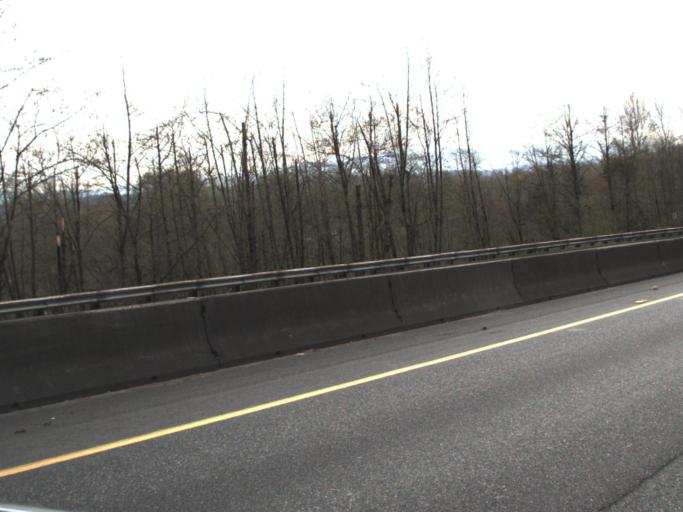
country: US
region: Washington
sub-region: King County
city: Kent
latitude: 47.3848
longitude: -122.2774
